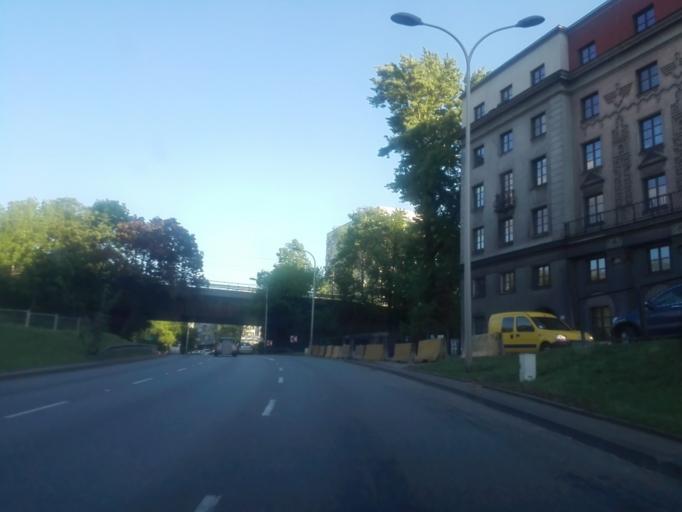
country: PL
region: Masovian Voivodeship
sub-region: Warszawa
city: Praga Polnoc
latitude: 52.2378
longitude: 21.0332
